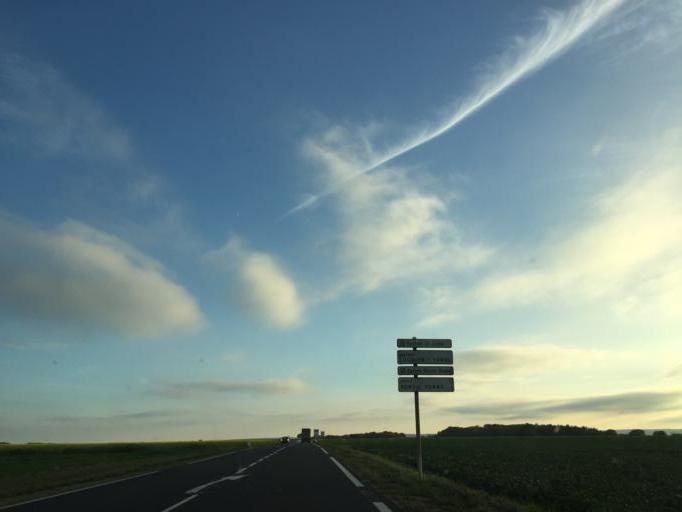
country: FR
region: Bourgogne
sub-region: Departement de l'Yonne
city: Sergines
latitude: 48.3502
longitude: 3.2318
